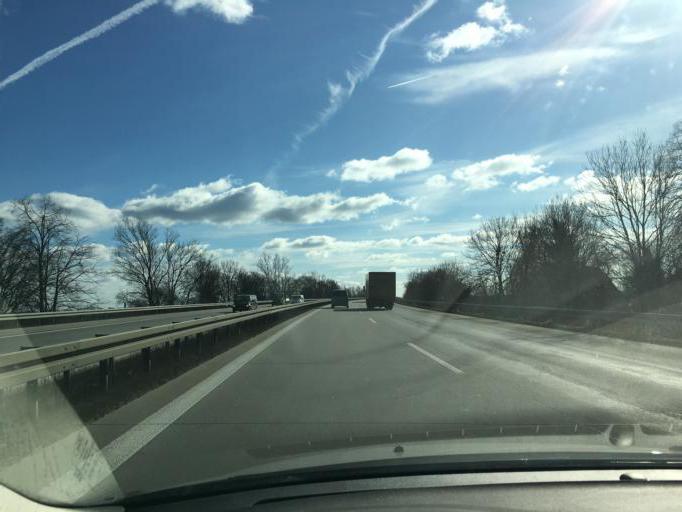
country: DE
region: Saxony
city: Borsdorf
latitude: 51.3477
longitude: 12.5053
